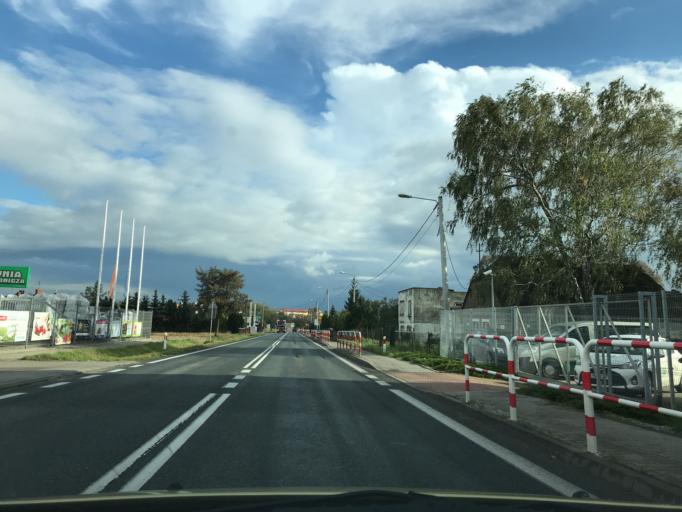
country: PL
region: Greater Poland Voivodeship
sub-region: Powiat ostrowski
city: Nowe Skalmierzyce
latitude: 51.7891
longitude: 18.0034
